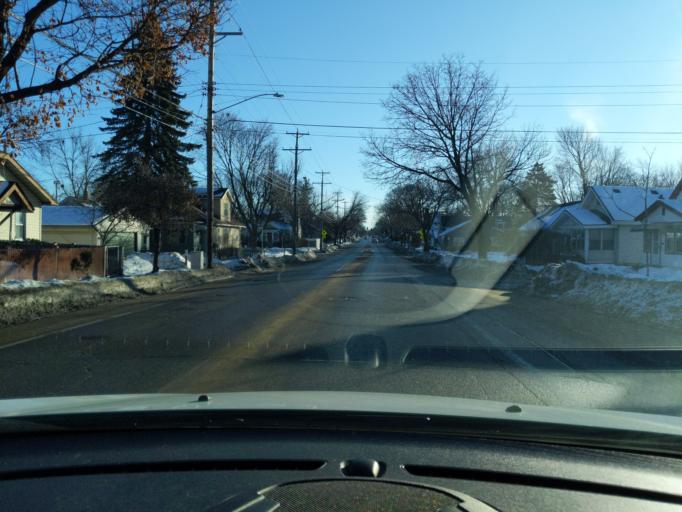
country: US
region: Minnesota
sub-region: Hennepin County
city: Minneapolis
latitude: 44.9269
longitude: -93.2357
